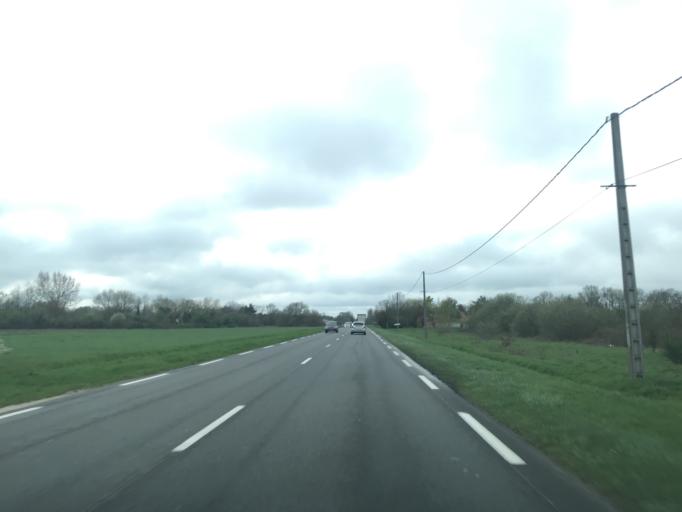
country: FR
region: Centre
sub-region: Departement du Loiret
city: Saint-Benoit-sur-Loire
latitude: 47.8473
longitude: 2.3084
